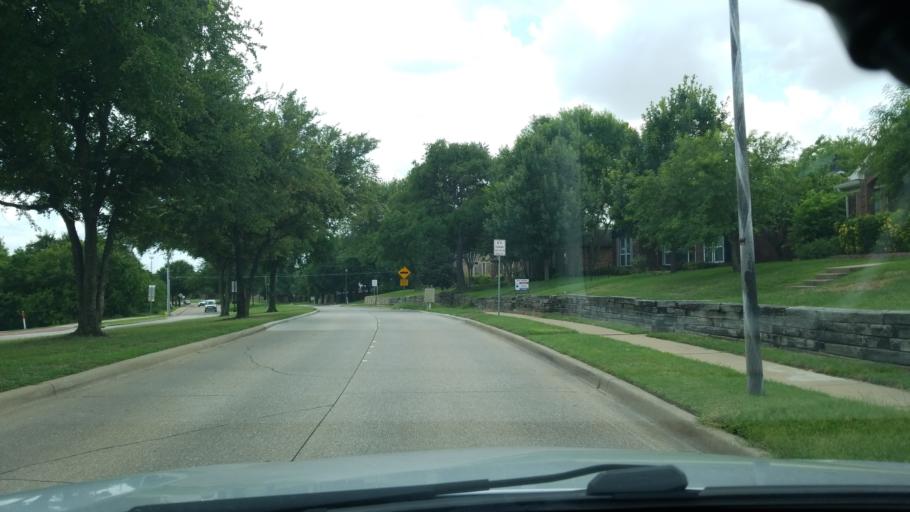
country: US
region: Texas
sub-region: Dallas County
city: Coppell
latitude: 32.9628
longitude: -96.9597
